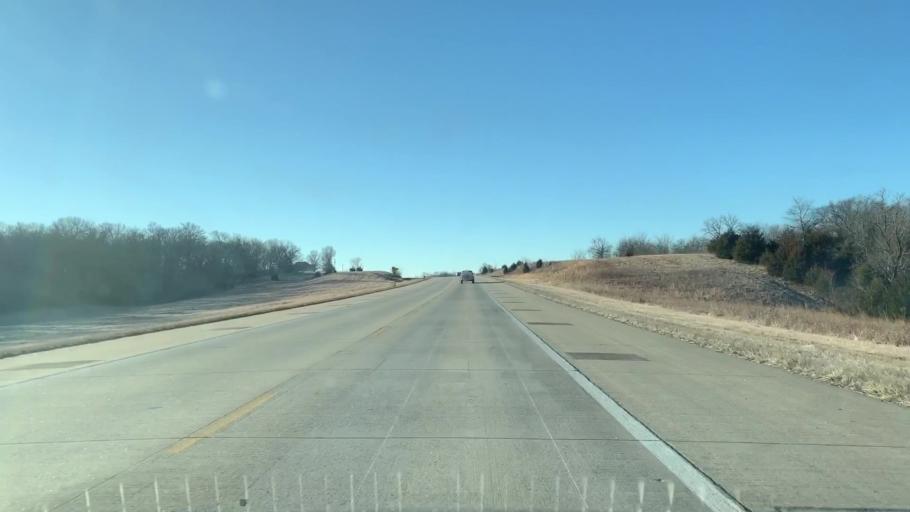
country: US
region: Kansas
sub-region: Crawford County
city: Arma
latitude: 37.5824
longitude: -94.7057
